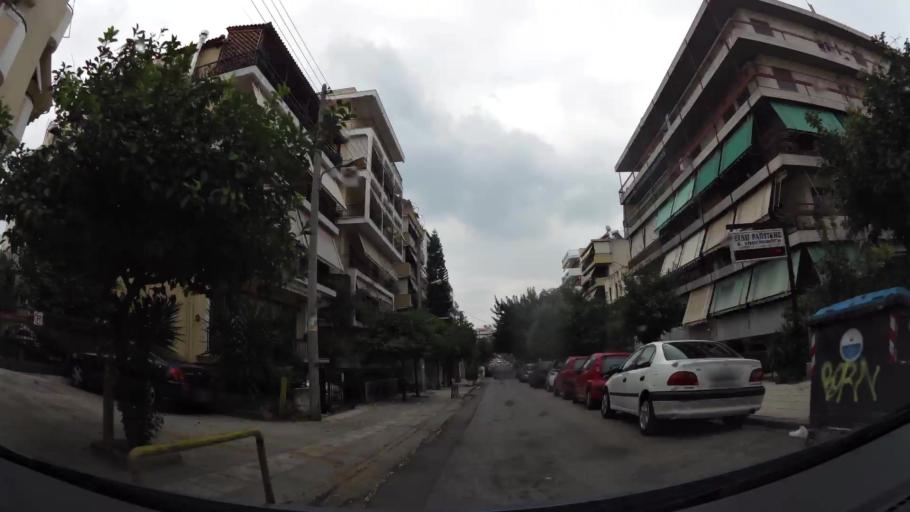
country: GR
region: Attica
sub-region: Nomarchia Athinas
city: Palaio Faliro
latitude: 37.9213
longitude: 23.7134
